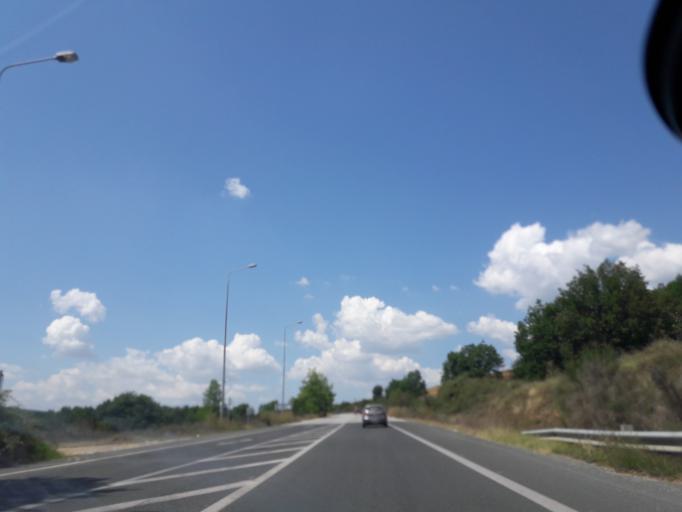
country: GR
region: Central Macedonia
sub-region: Nomos Chalkidikis
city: Galatista
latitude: 40.4651
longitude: 23.3674
